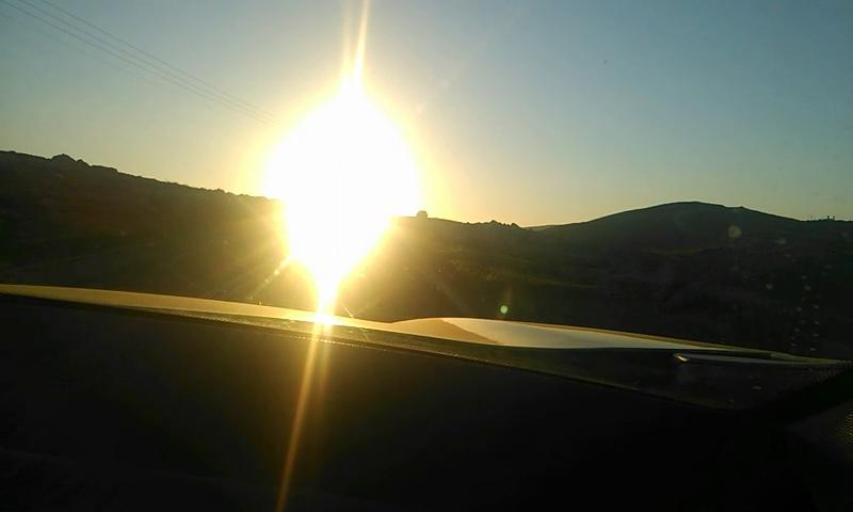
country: PS
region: West Bank
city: Rammun
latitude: 31.9200
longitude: 35.3299
